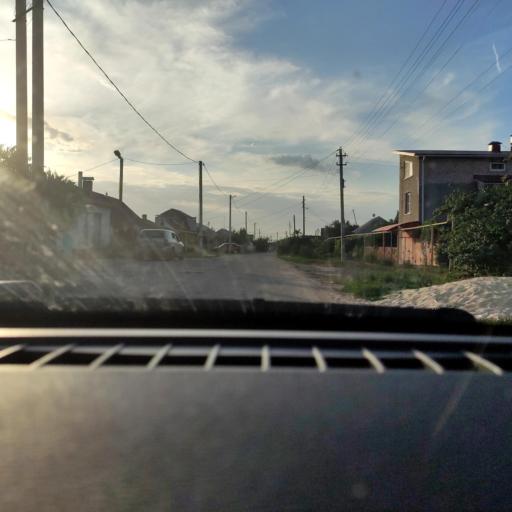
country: RU
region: Voronezj
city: Novaya Usman'
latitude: 51.6713
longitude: 39.3506
